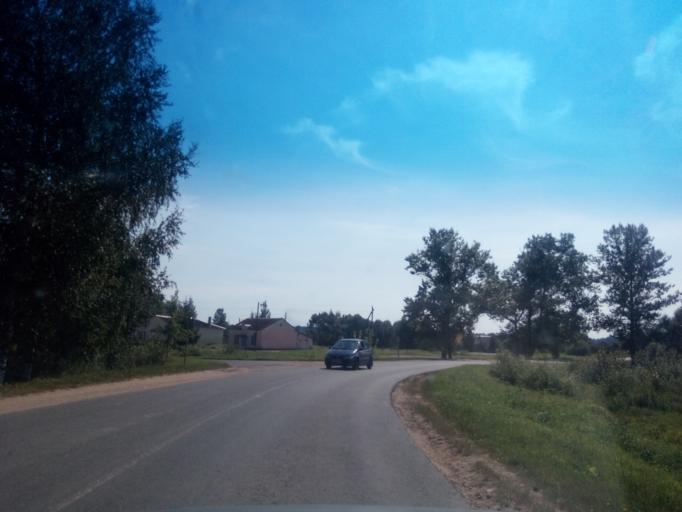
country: BY
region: Vitebsk
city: Vyerkhnyadzvinsk
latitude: 55.8342
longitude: 27.7355
